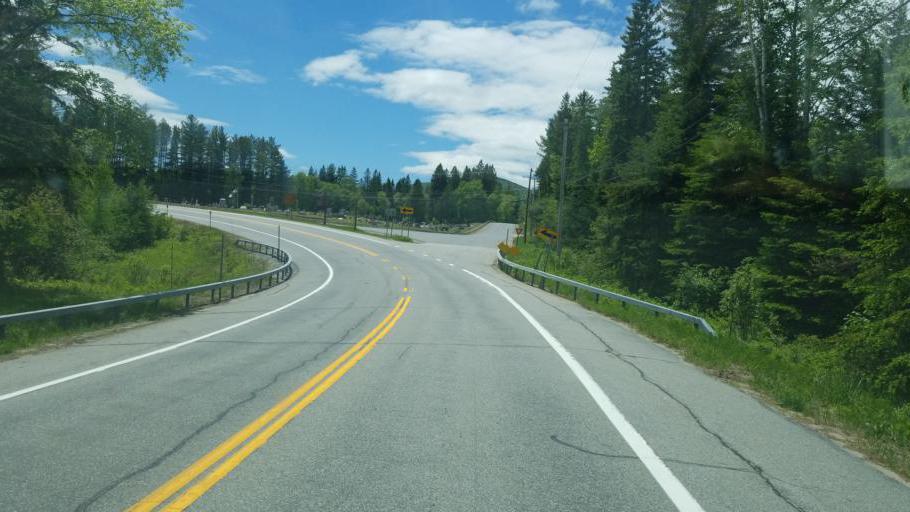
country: US
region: New York
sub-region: Hamilton County
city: Lake Pleasant
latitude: 43.7858
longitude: -74.3034
